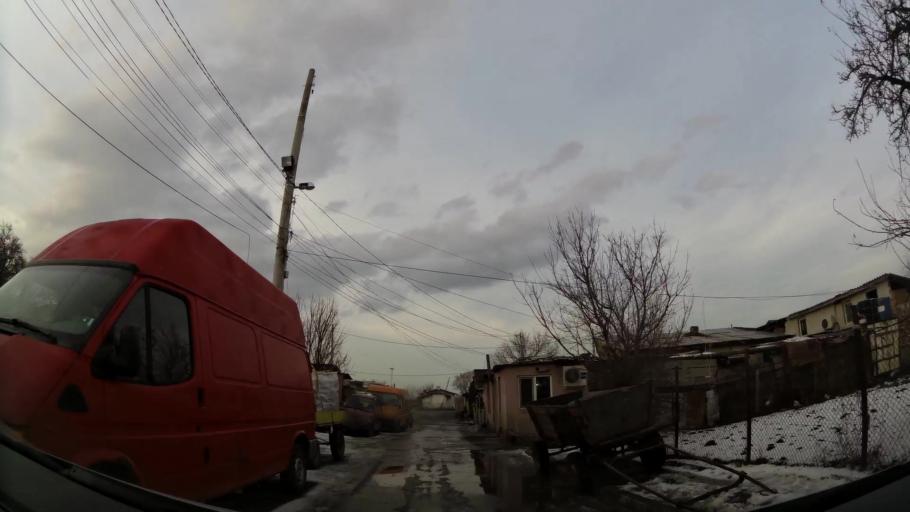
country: BG
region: Sofia-Capital
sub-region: Stolichna Obshtina
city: Sofia
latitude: 42.7260
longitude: 23.3469
